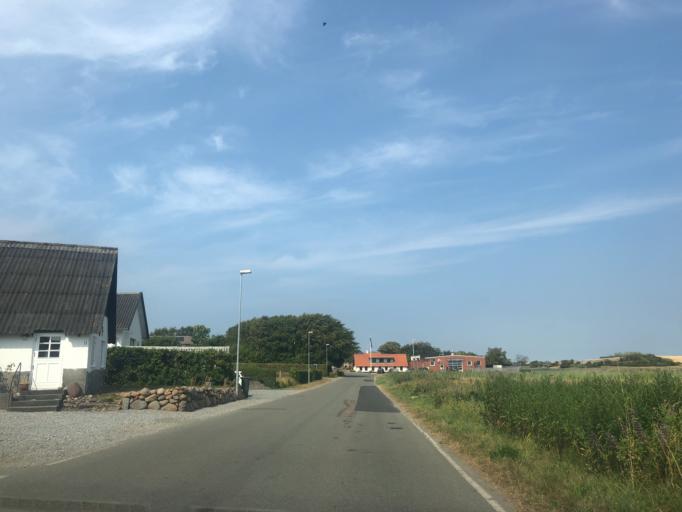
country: DK
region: North Denmark
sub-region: Morso Kommune
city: Nykobing Mors
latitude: 56.8172
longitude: 9.0273
